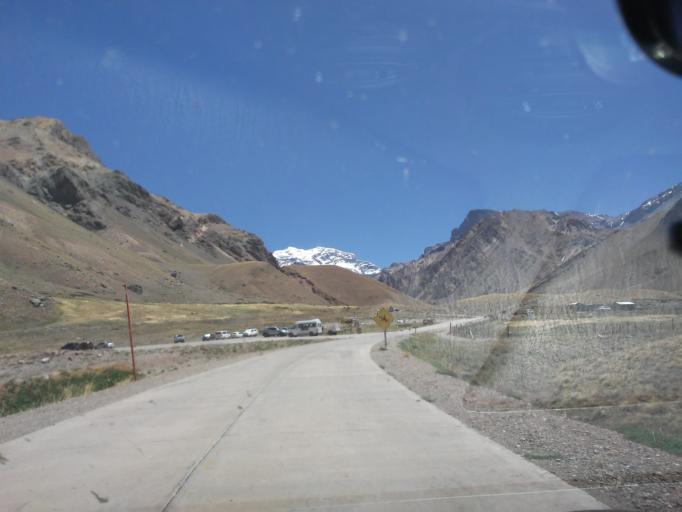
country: CL
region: Valparaiso
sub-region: Provincia de Los Andes
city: Los Andes
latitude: -32.8126
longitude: -69.9424
